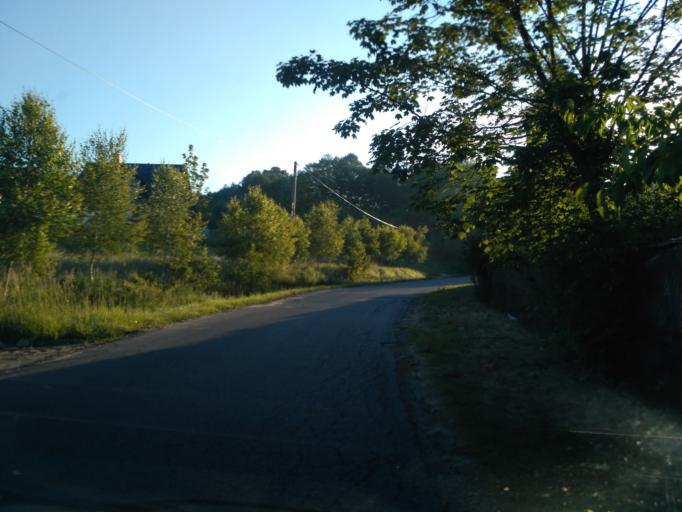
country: PL
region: Subcarpathian Voivodeship
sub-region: Powiat strzyzowski
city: Polomia
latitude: 49.8994
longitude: 21.8834
